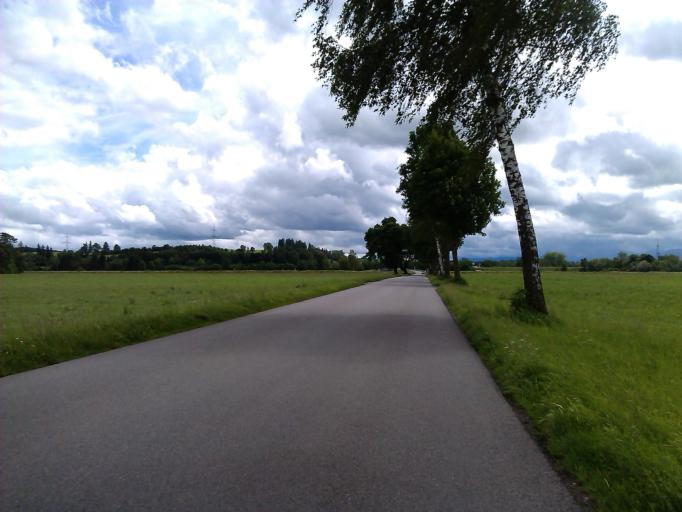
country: DE
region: Bavaria
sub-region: Swabia
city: Biessenhofen
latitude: 47.8086
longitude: 10.6213
